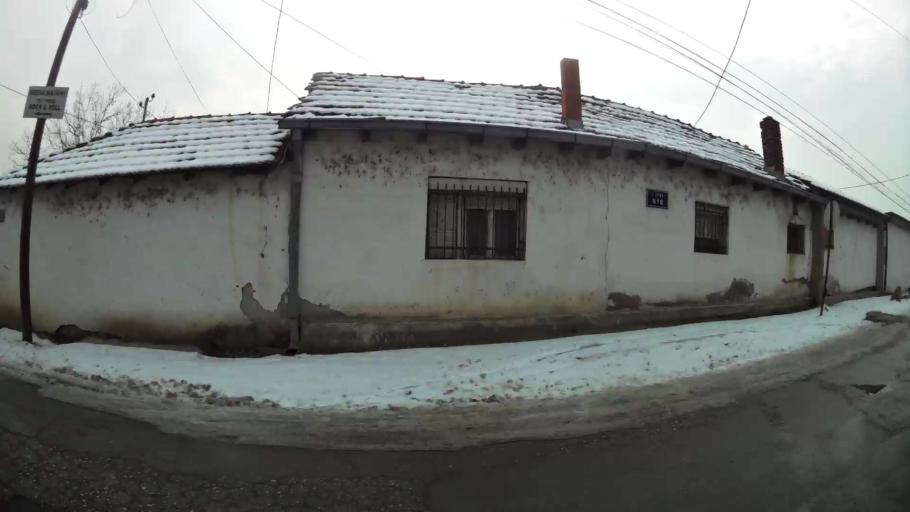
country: MK
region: Cair
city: Cair
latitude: 41.9964
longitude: 21.4647
